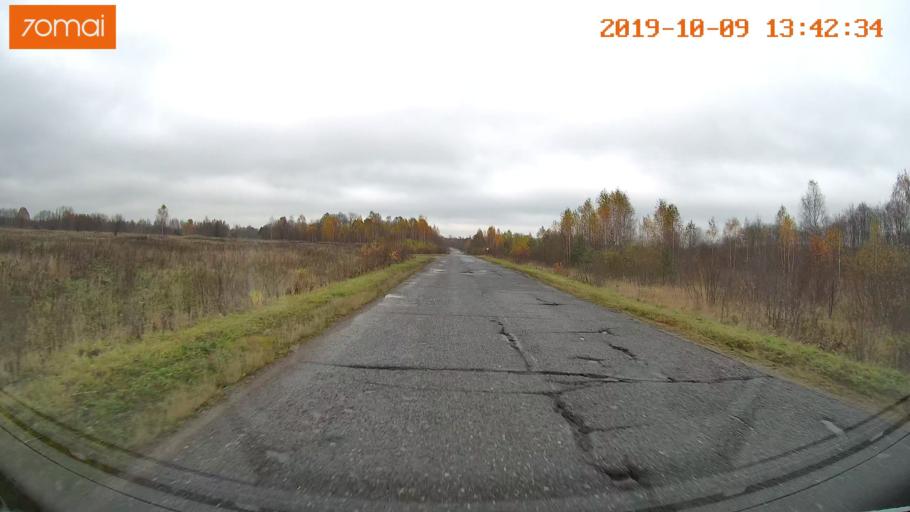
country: RU
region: Kostroma
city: Buy
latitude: 58.3552
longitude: 41.1884
